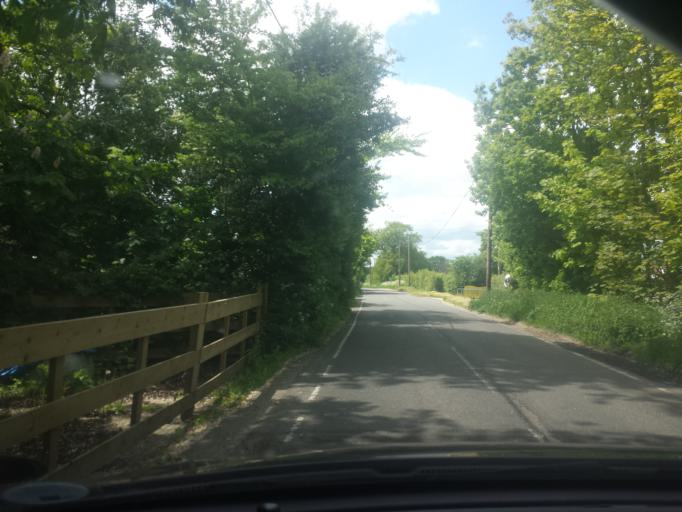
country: GB
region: England
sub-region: Essex
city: Little Clacton
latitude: 51.8814
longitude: 1.1621
